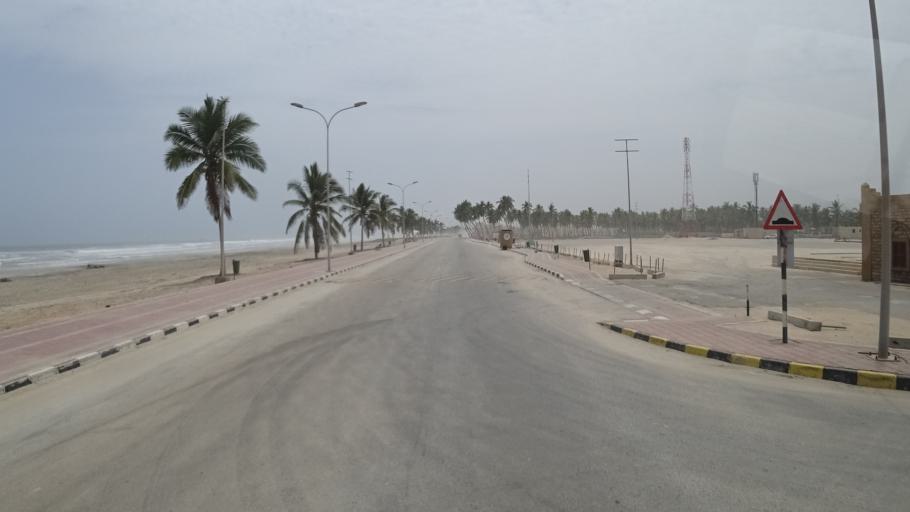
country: OM
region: Zufar
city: Salalah
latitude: 17.0343
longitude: 54.3952
